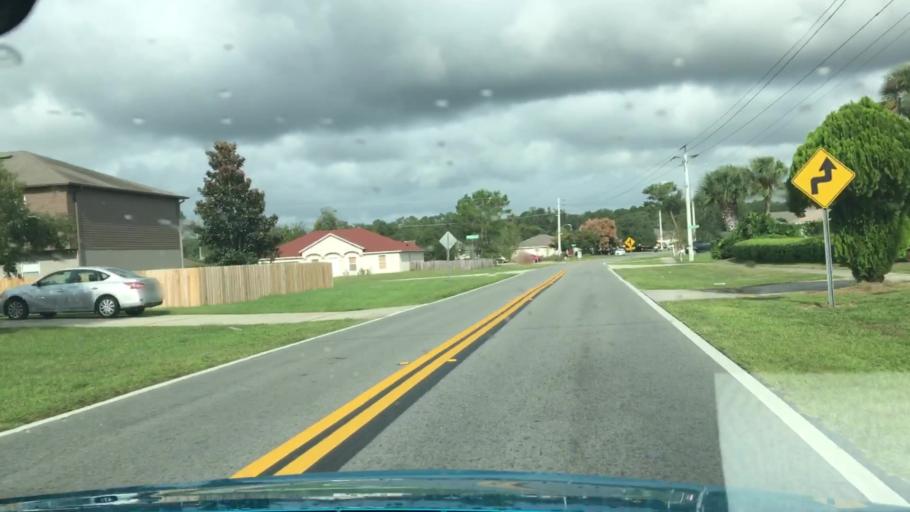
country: US
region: Florida
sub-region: Volusia County
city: Lake Helen
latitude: 28.9492
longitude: -81.1856
